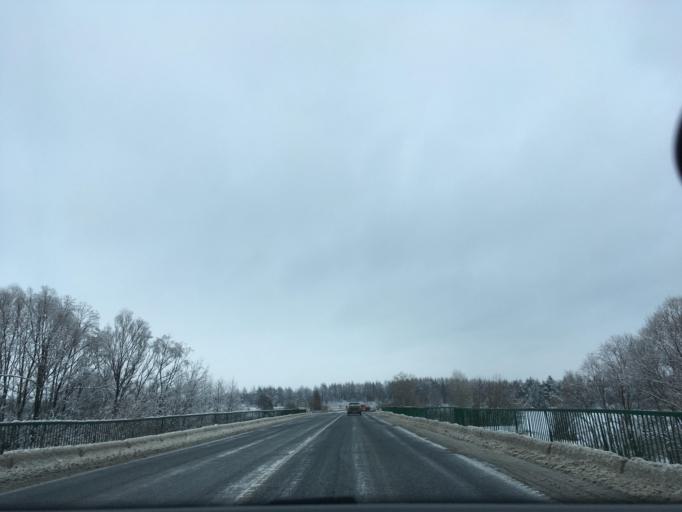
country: RU
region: Voronezj
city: Zabolotovka
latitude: 50.2455
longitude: 39.3793
